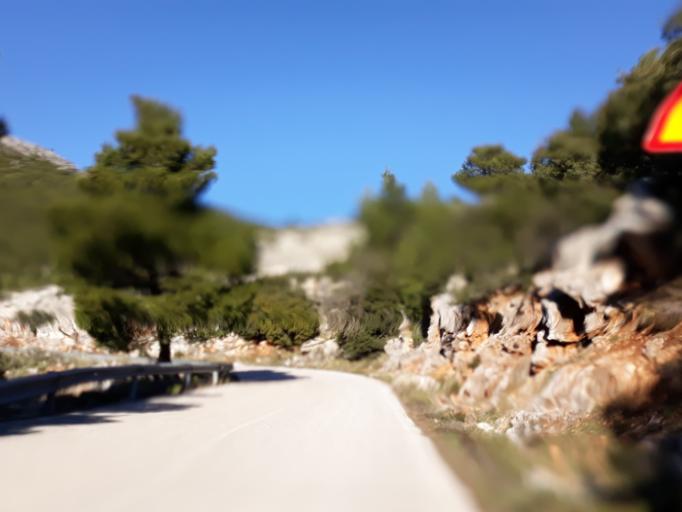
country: GR
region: Attica
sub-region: Nomarchia Dytikis Attikis
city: Fyli
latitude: 38.1430
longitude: 23.6453
